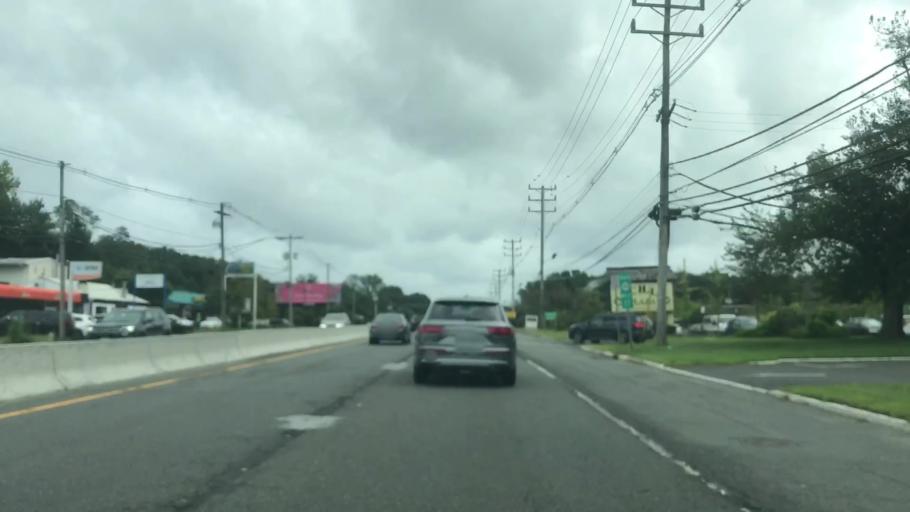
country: US
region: New Jersey
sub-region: Monmouth County
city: Oakhurst
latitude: 40.2578
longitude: -74.0407
